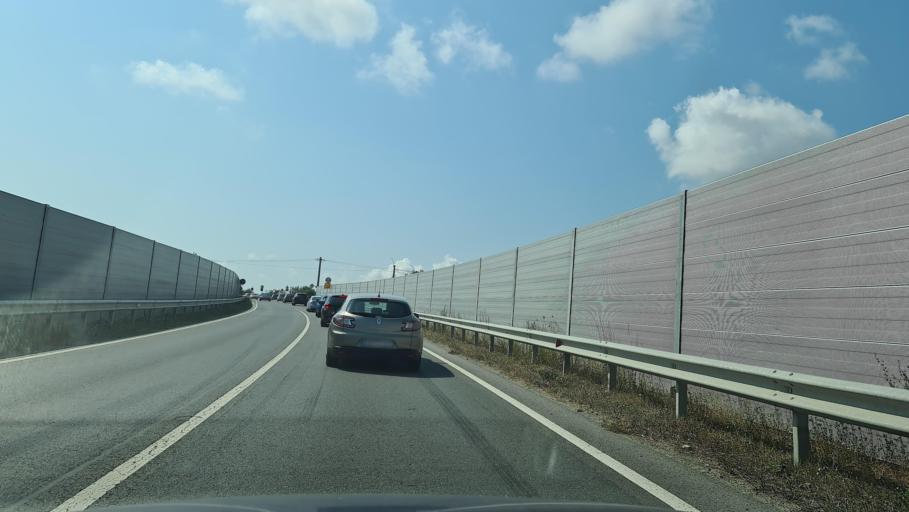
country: RO
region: Constanta
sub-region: Comuna Agigea
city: Agigea
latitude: 44.0944
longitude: 28.6387
